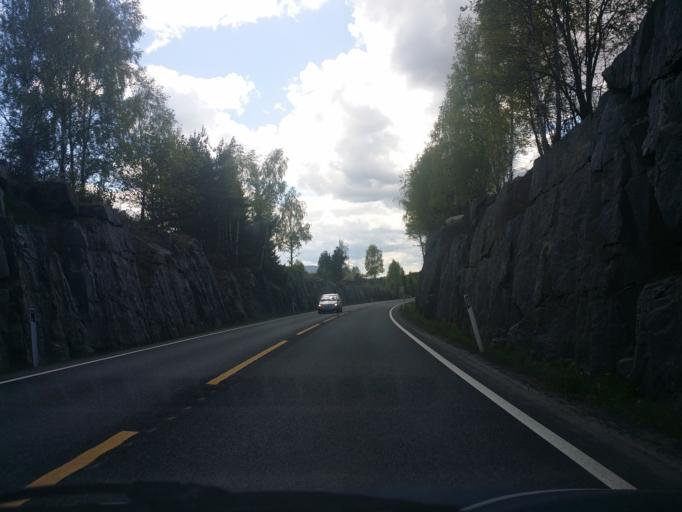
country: NO
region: Buskerud
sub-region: Modum
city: Vikersund
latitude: 59.9700
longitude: 9.9868
